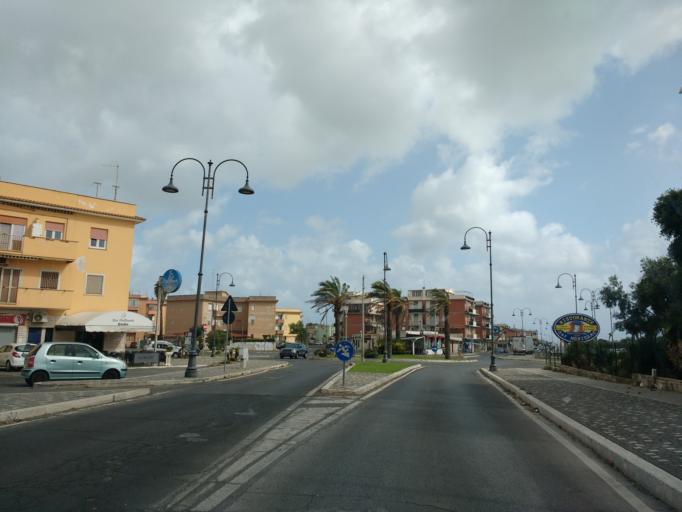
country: IT
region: Latium
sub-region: Citta metropolitana di Roma Capitale
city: Anzio
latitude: 41.4664
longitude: 12.6107
